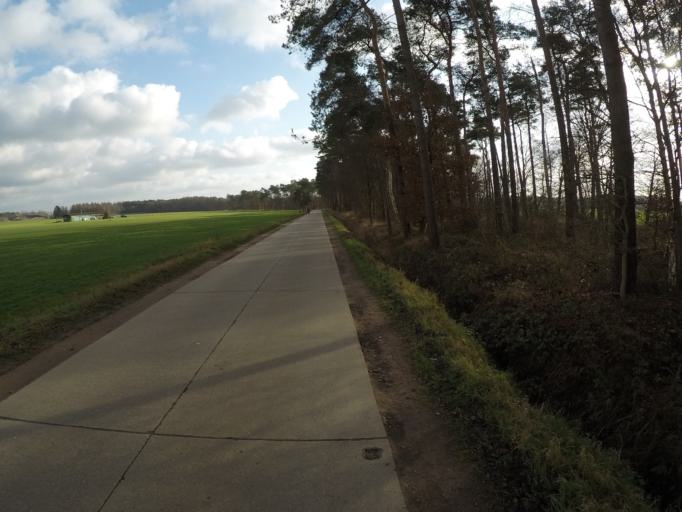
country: BE
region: Flanders
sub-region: Provincie Antwerpen
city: Vorselaar
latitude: 51.2413
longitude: 4.7533
